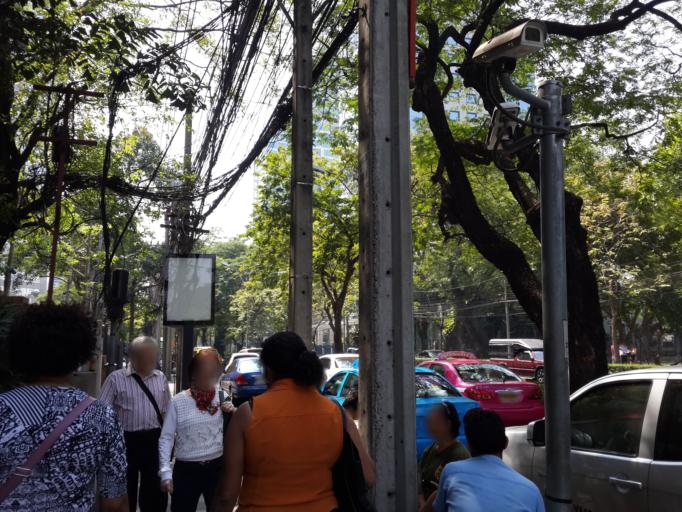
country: TH
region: Bangkok
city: Ratchathewi
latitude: 13.7403
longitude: 100.5471
